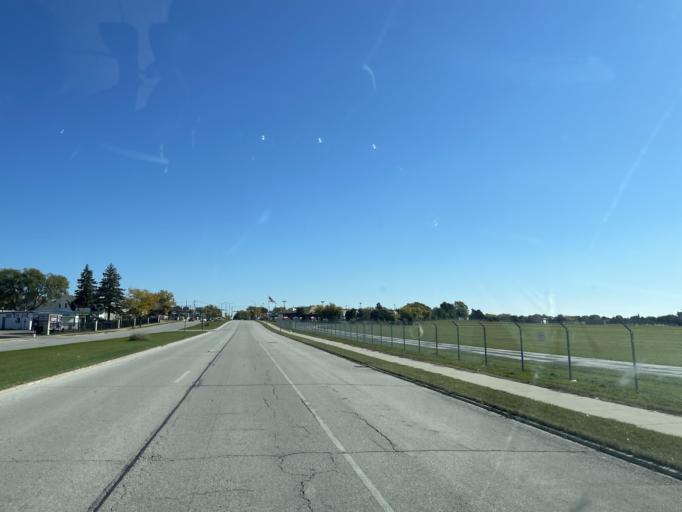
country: US
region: Wisconsin
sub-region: Waukesha County
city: Butler
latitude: 43.1150
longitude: -88.0291
